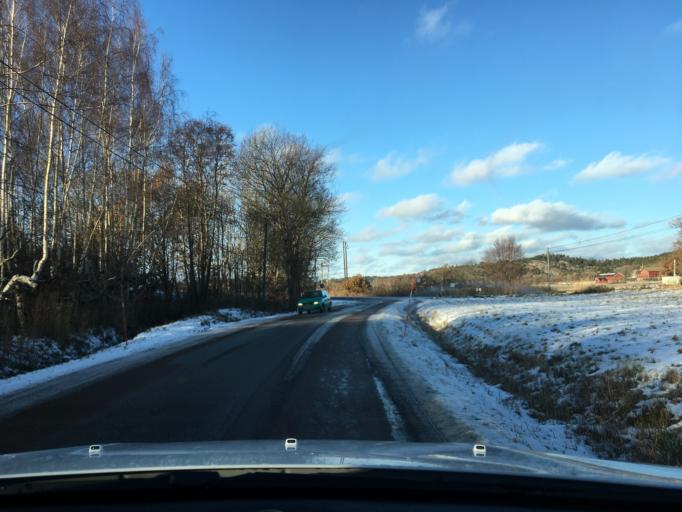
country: SE
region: Vaestra Goetaland
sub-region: Tjorns Kommun
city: Myggenas
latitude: 58.0999
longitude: 11.7093
